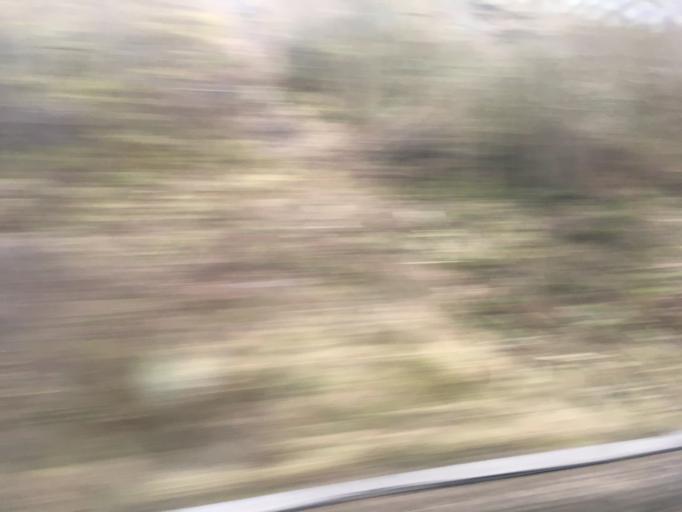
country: GB
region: England
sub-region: South Gloucestershire
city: Chipping Sodbury
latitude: 51.5327
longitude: -2.3902
